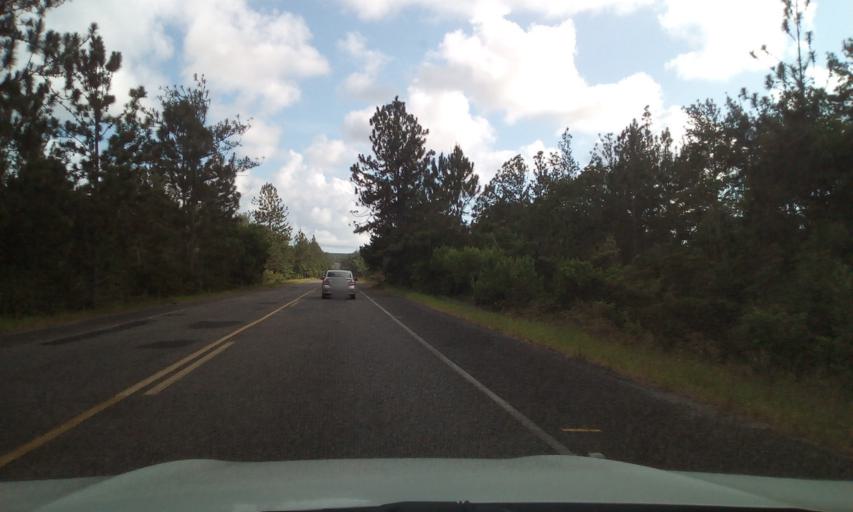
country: BR
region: Bahia
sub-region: Entre Rios
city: Entre Rios
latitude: -12.1511
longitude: -37.8001
